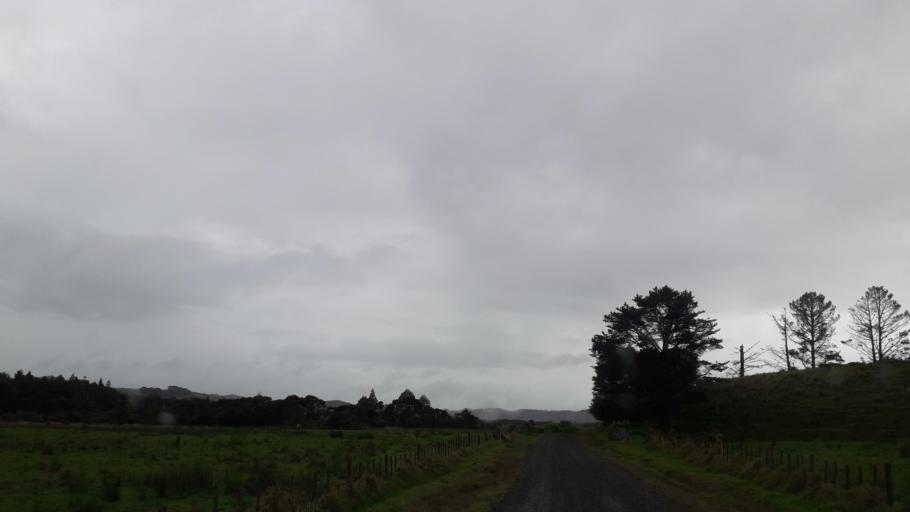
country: NZ
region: Northland
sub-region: Far North District
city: Kaitaia
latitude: -35.3947
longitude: 173.4074
